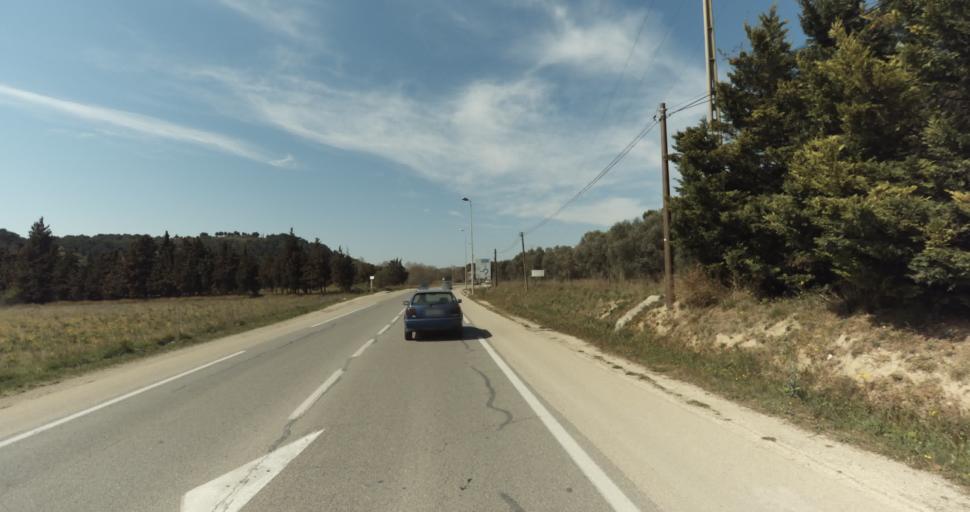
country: FR
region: Provence-Alpes-Cote d'Azur
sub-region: Departement des Bouches-du-Rhone
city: Velaux
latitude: 43.5414
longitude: 5.2622
